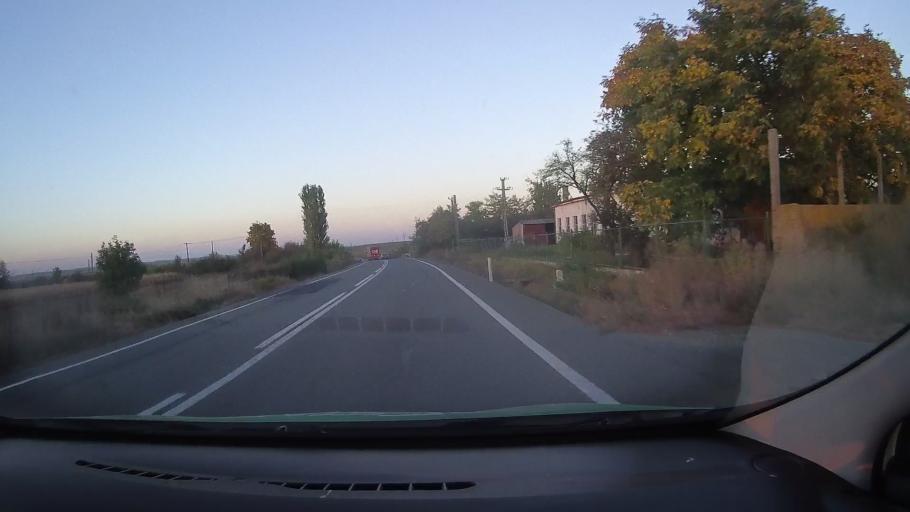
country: RO
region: Bihor
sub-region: Comuna Cherechiu
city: Cherechiu
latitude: 47.3830
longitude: 22.1431
